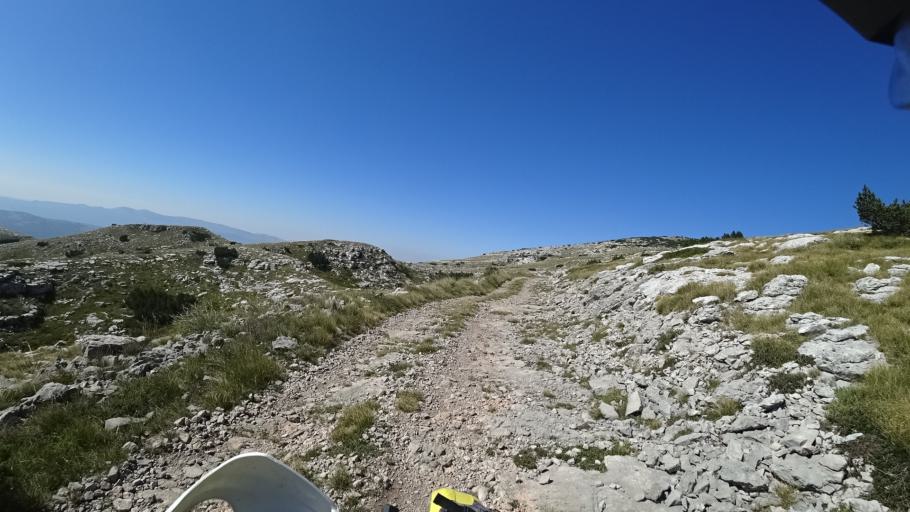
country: HR
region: Splitsko-Dalmatinska
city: Hrvace
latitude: 43.9309
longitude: 16.6028
